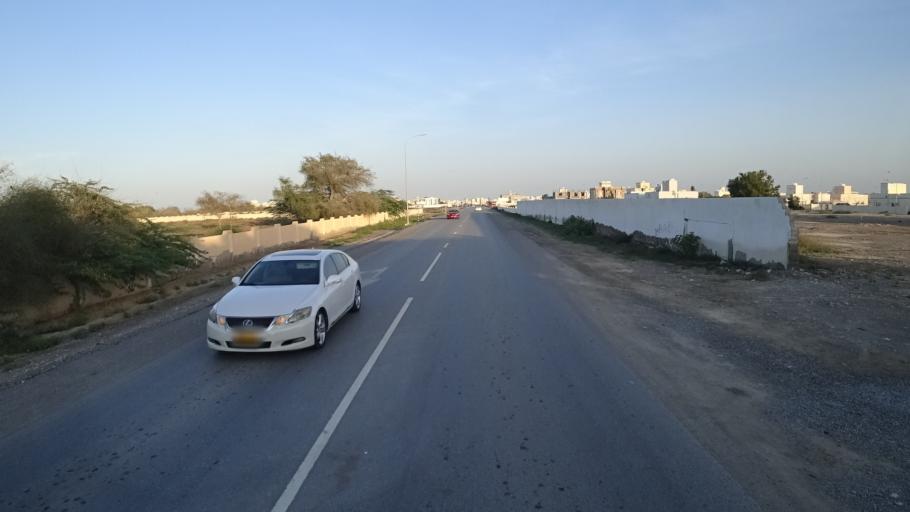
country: OM
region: Al Batinah
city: Barka'
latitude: 23.7049
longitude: 57.9057
